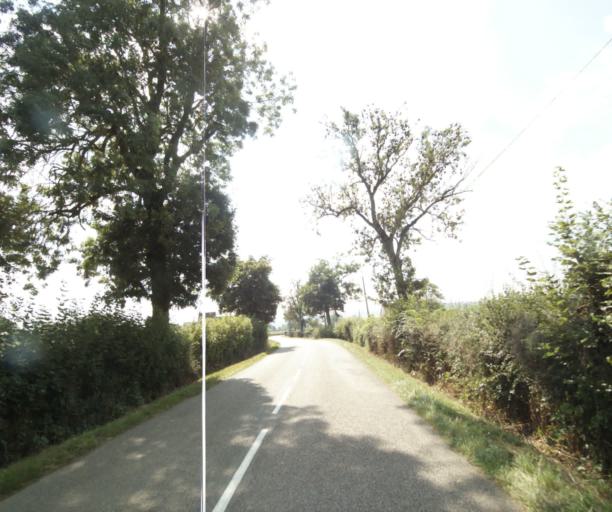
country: FR
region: Bourgogne
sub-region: Departement de Saone-et-Loire
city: Charolles
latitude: 46.3759
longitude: 4.2486
